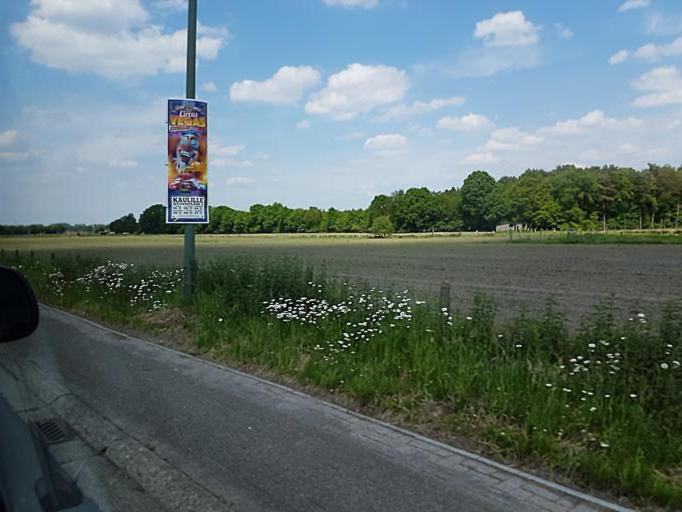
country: BE
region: Flanders
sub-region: Provincie Limburg
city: Neerpelt
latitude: 51.2089
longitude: 5.4991
